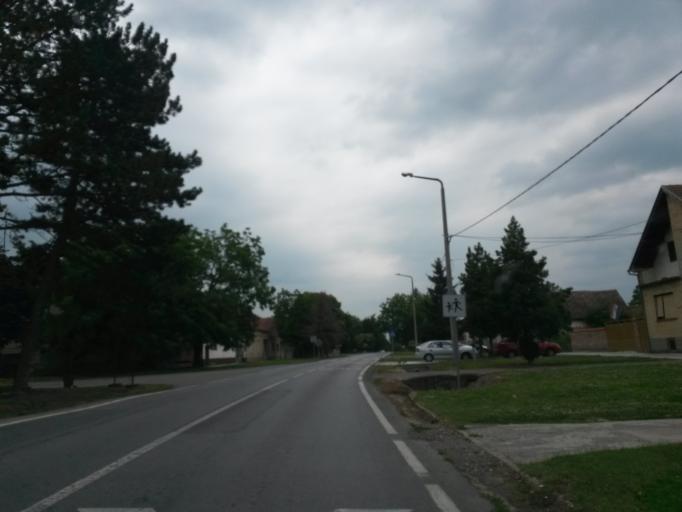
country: HR
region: Vukovarsko-Srijemska
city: Lovas
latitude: 45.2948
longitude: 19.0986
